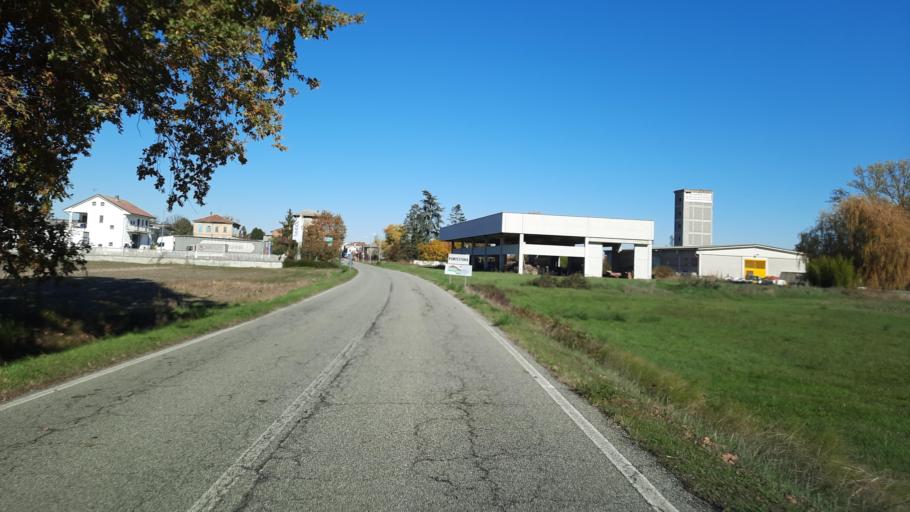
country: IT
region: Piedmont
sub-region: Provincia di Alessandria
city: Pontestura
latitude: 45.1371
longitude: 8.3351
